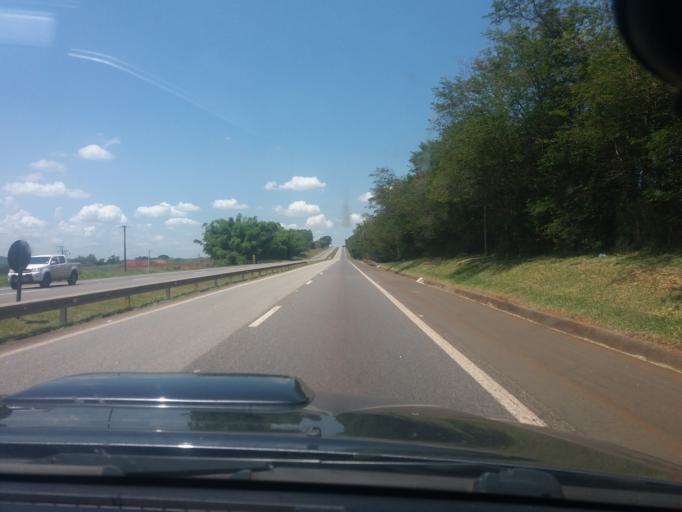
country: BR
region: Sao Paulo
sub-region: Tatui
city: Tatui
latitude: -23.4176
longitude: -47.9288
